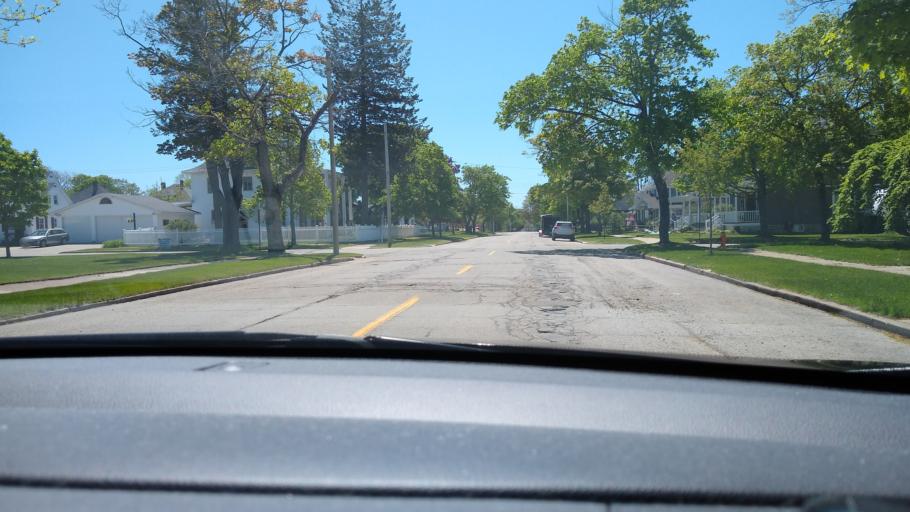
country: US
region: Michigan
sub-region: Delta County
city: Escanaba
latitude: 45.7387
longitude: -87.0612
